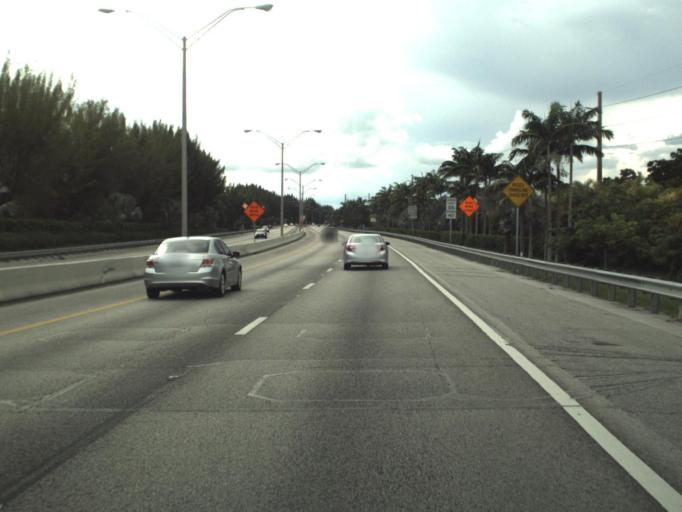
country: US
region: Florida
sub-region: Miami-Dade County
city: Glenvar Heights
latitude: 25.6954
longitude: -80.3202
